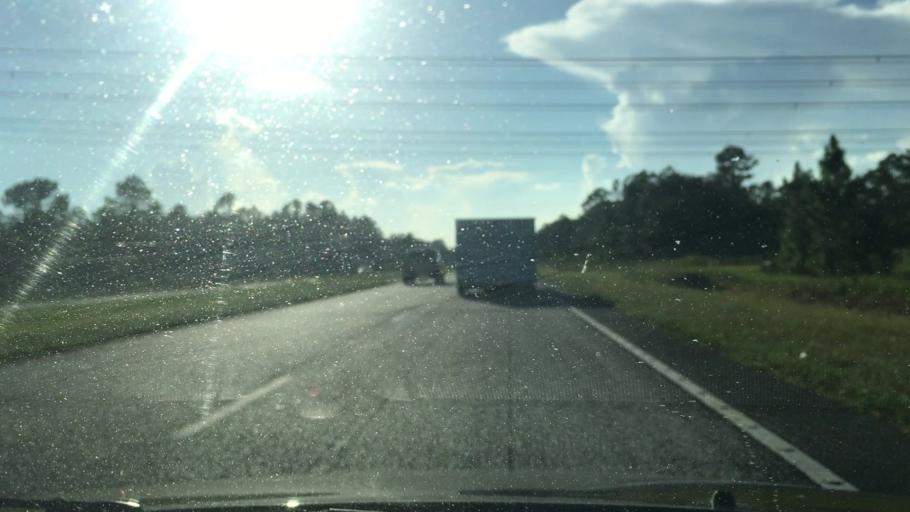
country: US
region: Florida
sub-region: Orange County
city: Christmas
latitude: 28.5363
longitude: -81.0568
